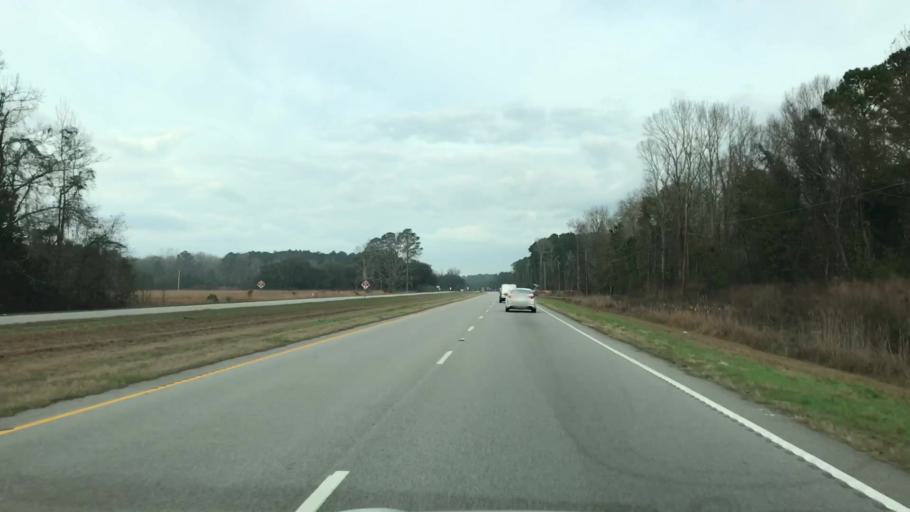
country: US
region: South Carolina
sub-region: Hampton County
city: Yemassee
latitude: 32.6350
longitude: -80.8411
